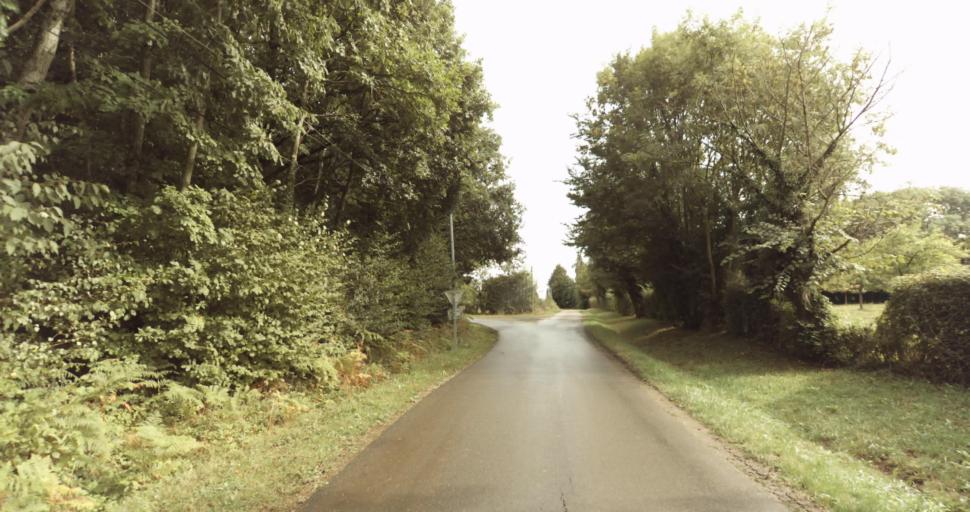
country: FR
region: Lower Normandy
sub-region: Departement de l'Orne
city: Vimoutiers
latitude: 48.8647
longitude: 0.1848
